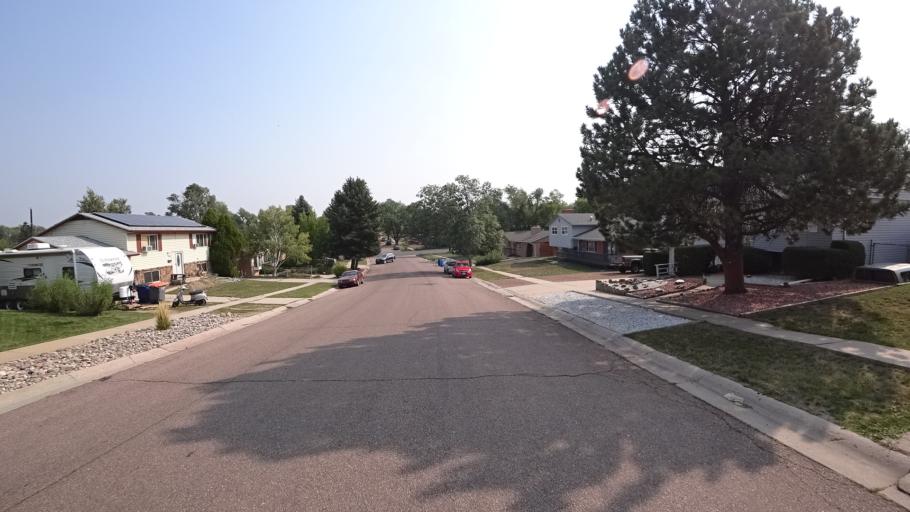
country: US
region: Colorado
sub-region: El Paso County
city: Stratmoor
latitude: 38.8109
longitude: -104.7773
